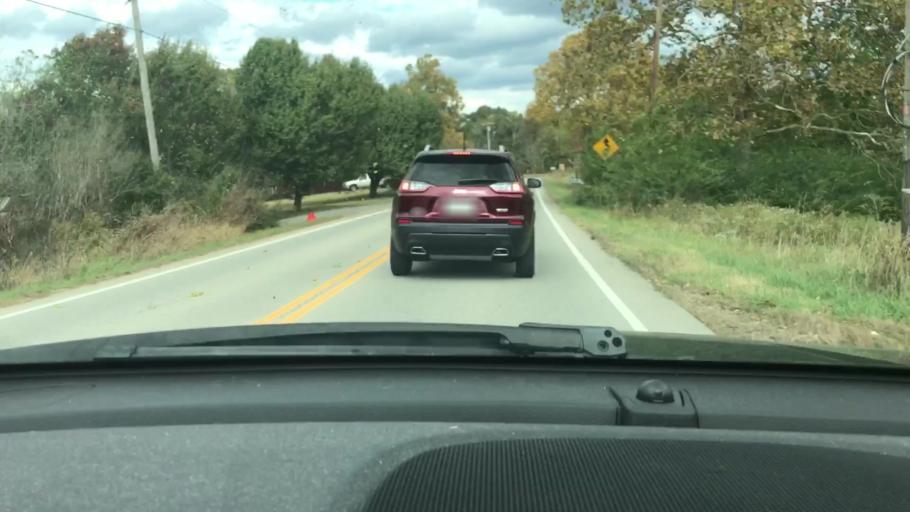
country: US
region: Tennessee
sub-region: Dickson County
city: Charlotte
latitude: 36.2596
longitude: -87.2214
